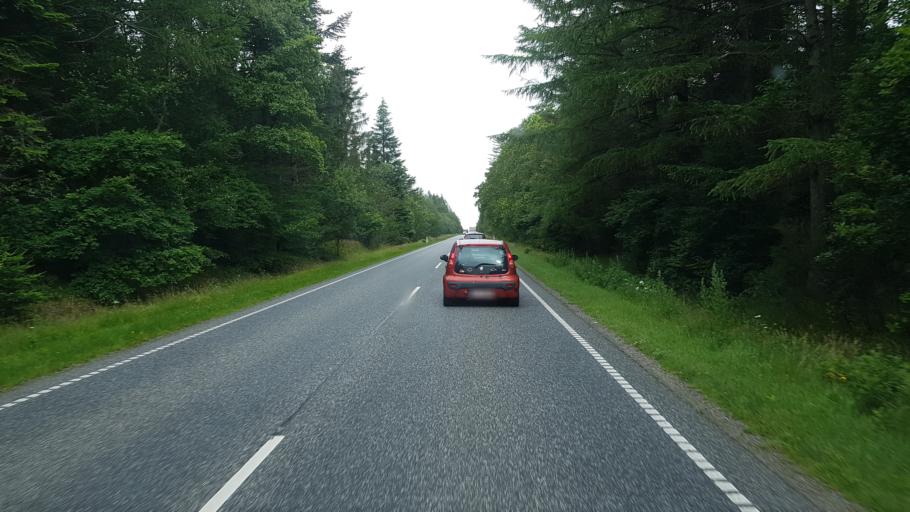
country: DK
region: Central Jutland
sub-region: Lemvig Kommune
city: Lemvig
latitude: 56.4653
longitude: 8.3222
